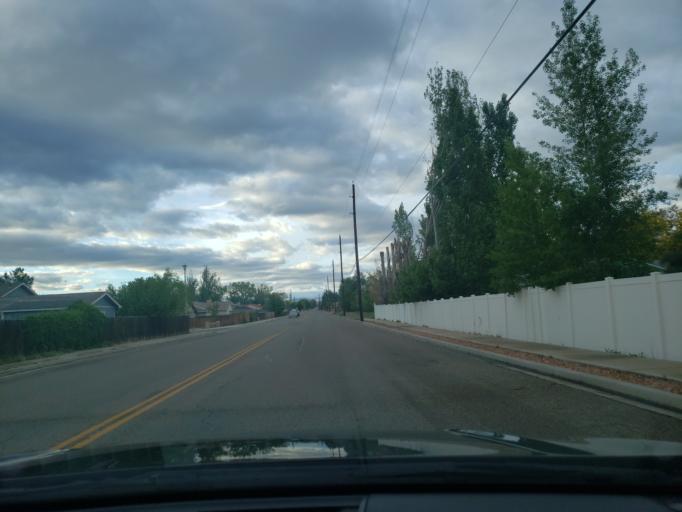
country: US
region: Colorado
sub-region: Mesa County
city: Fruita
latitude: 39.1692
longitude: -108.7290
